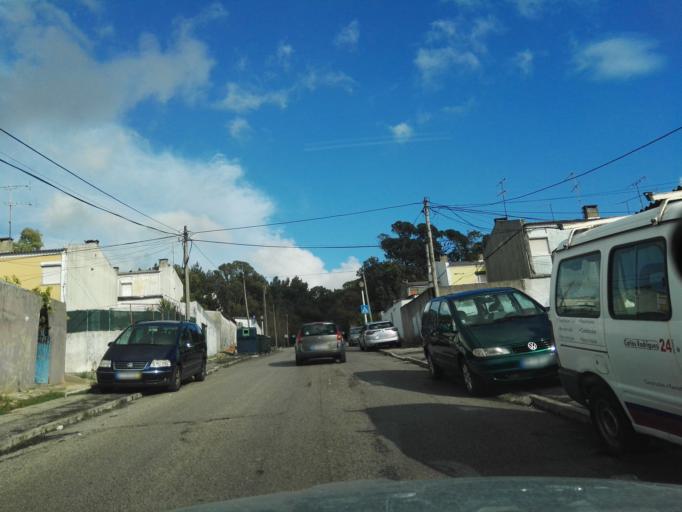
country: PT
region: Lisbon
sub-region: Amadora
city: Amadora
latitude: 38.7325
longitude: -9.2047
